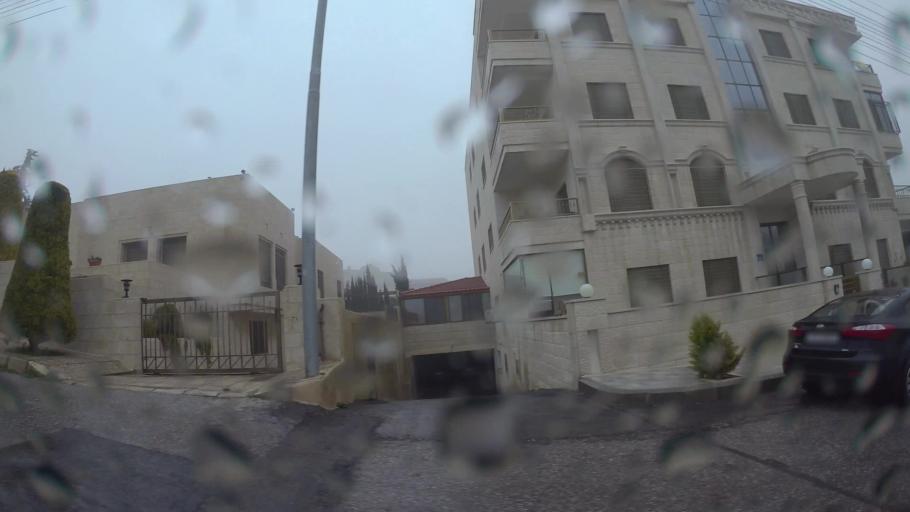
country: JO
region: Amman
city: Al Jubayhah
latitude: 32.0143
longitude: 35.8882
